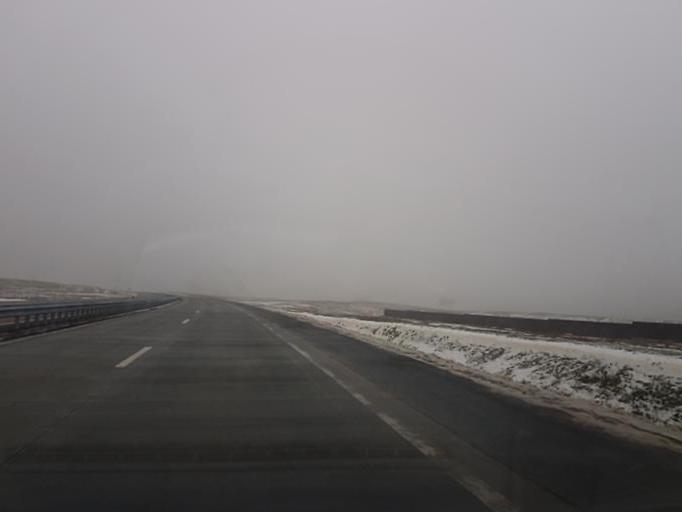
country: BY
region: Minsk
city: Atolina
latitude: 53.7581
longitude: 27.4057
